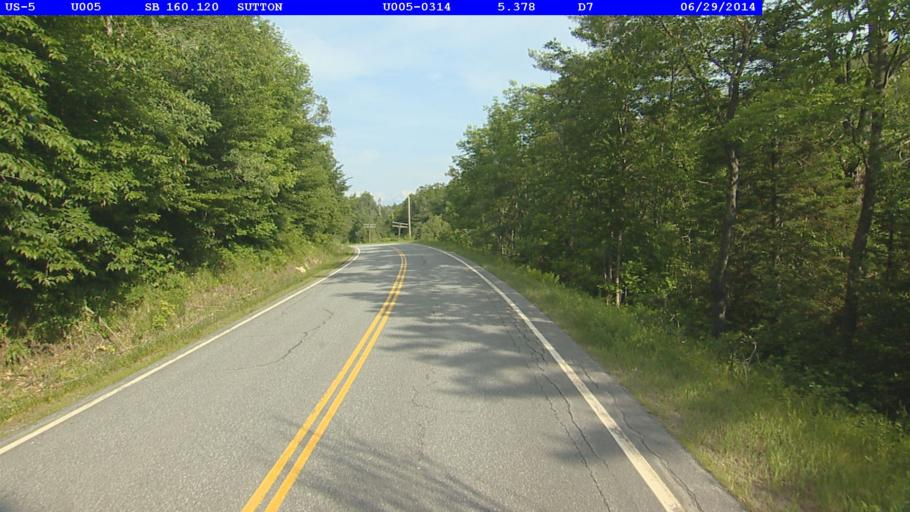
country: US
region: Vermont
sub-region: Caledonia County
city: Lyndonville
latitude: 44.6910
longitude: -72.0594
